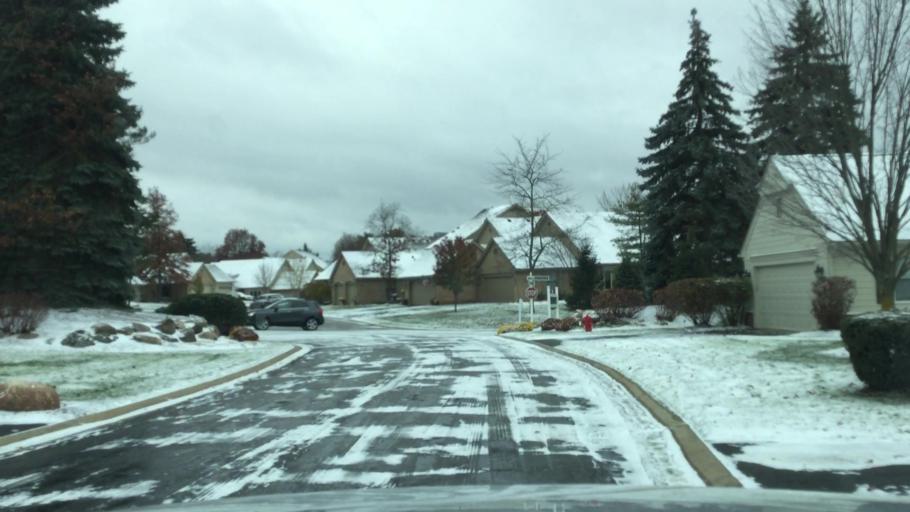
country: US
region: Michigan
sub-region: Livingston County
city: Brighton
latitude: 42.5306
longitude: -83.8541
